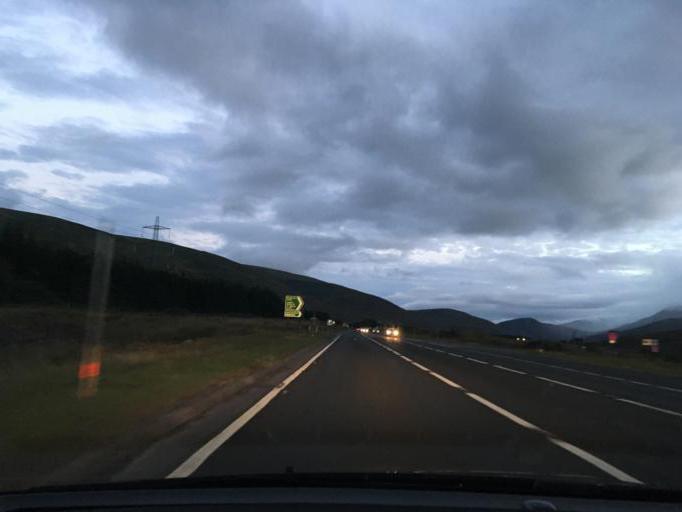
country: GB
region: Scotland
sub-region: Highland
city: Kingussie
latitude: 56.9179
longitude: -4.2359
